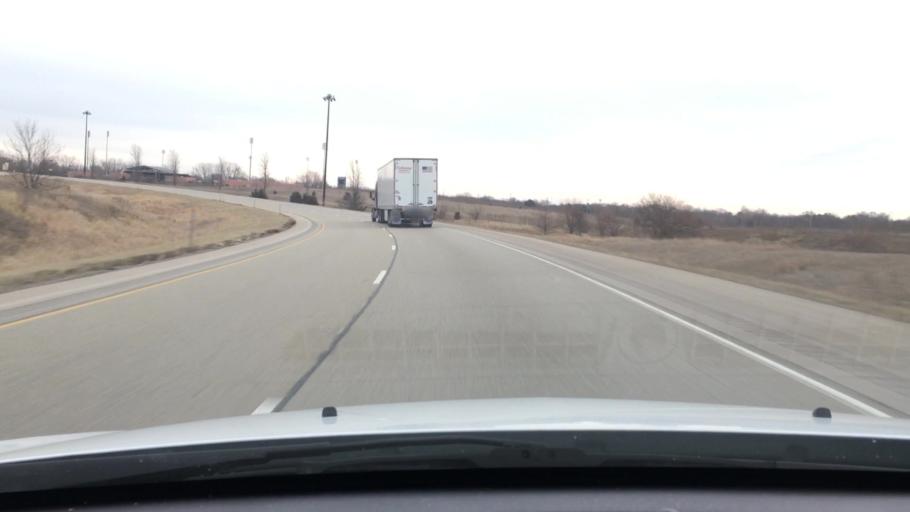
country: US
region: Illinois
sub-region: McLean County
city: Normal
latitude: 40.5357
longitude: -89.0105
